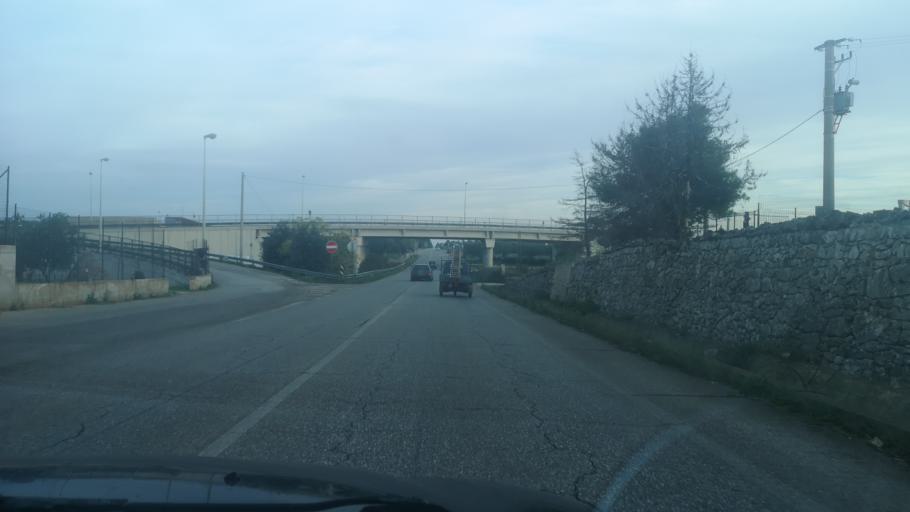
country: IT
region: Apulia
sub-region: Provincia di Bari
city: Cassano delle Murge
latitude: 40.8991
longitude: 16.7736
